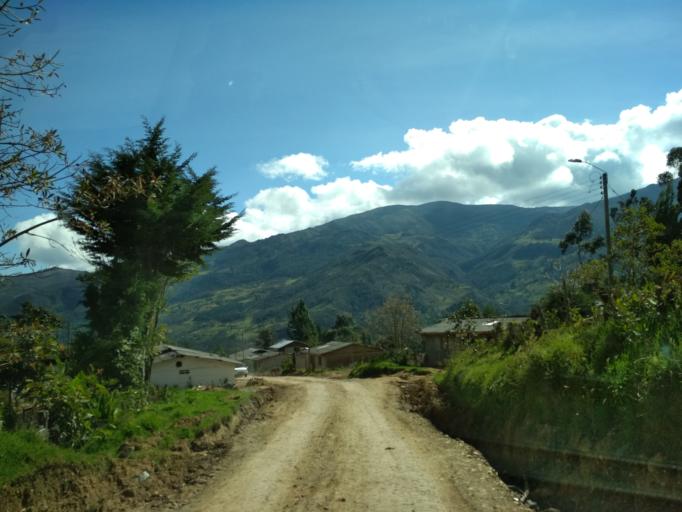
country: CO
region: Cauca
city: Jambalo
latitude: 2.7092
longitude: -76.3285
